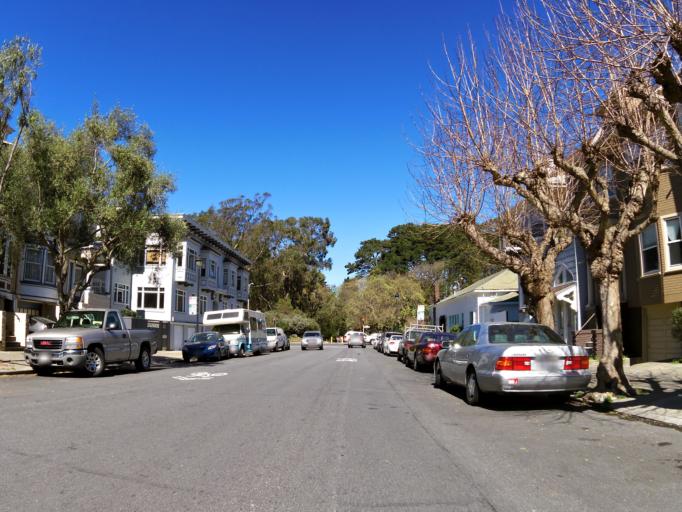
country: US
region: California
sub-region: San Francisco County
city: San Francisco
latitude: 37.7654
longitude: -122.4622
